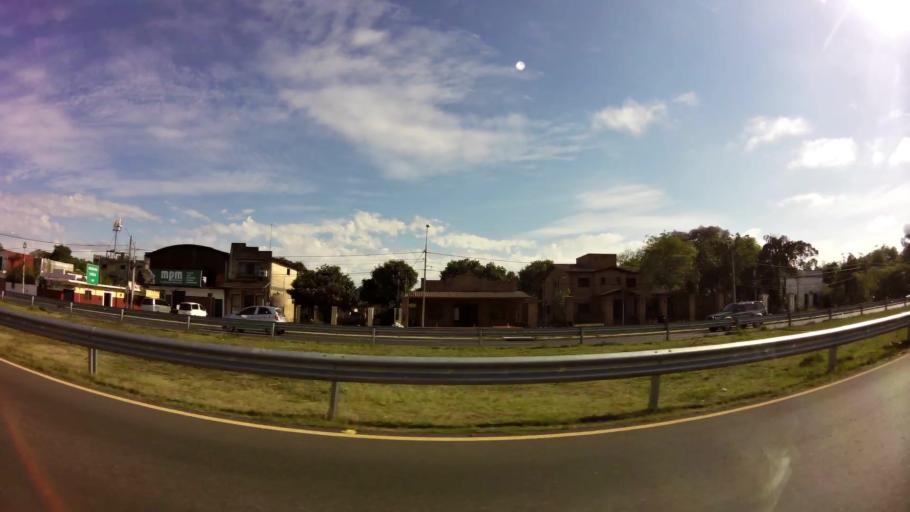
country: PY
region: Central
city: Fernando de la Mora
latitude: -25.2567
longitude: -57.5526
